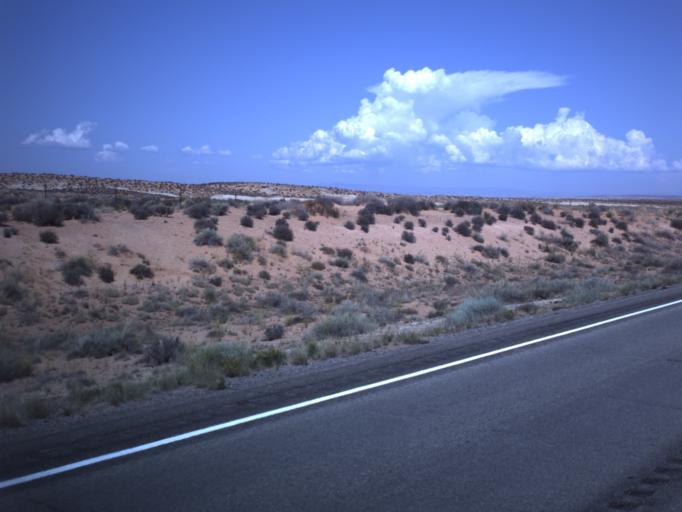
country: US
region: Utah
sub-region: San Juan County
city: Blanding
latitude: 37.0763
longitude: -109.5485
